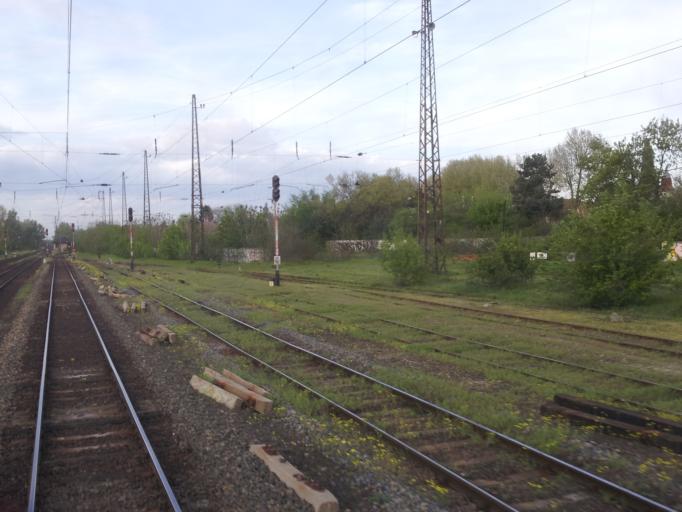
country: HU
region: Budapest
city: Budapest XV. keruelet
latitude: 47.5696
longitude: 19.1142
